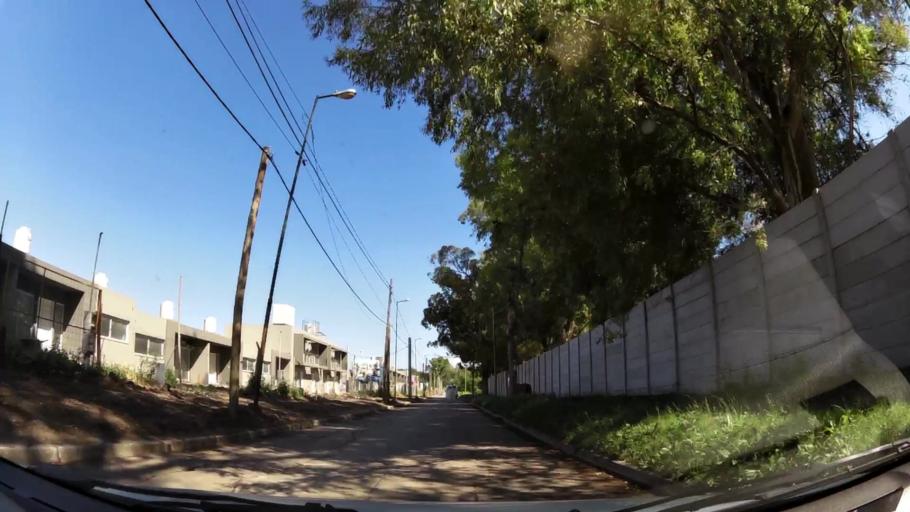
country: AR
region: Buenos Aires
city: Ituzaingo
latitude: -34.6224
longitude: -58.6632
